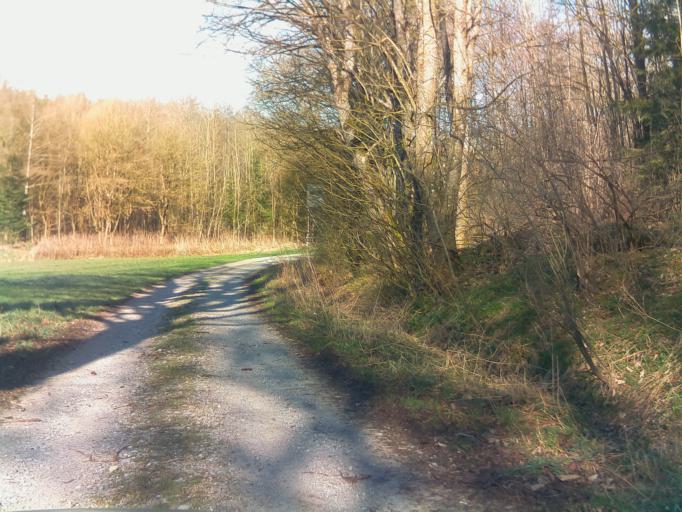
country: DE
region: Bavaria
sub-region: Swabia
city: Grossaitingen
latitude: 48.2486
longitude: 10.7458
